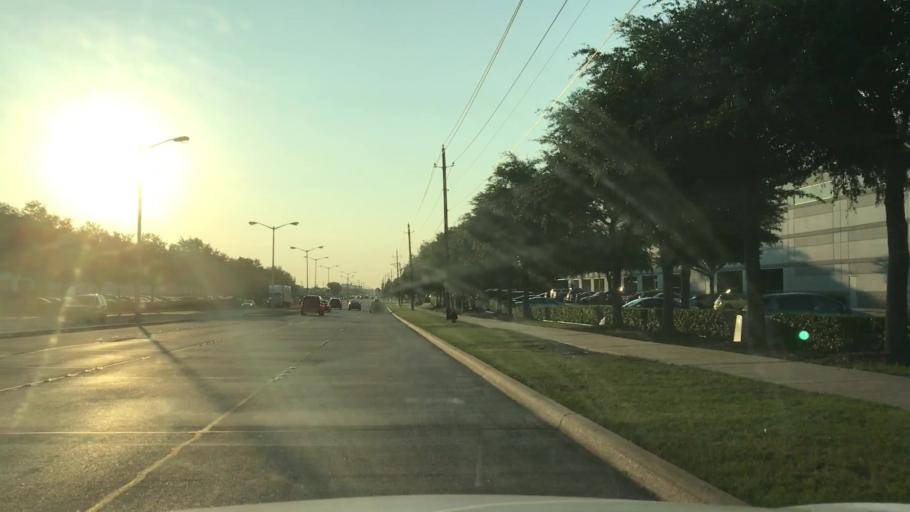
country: US
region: Texas
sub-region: Dallas County
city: Garland
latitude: 32.8944
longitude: -96.6901
